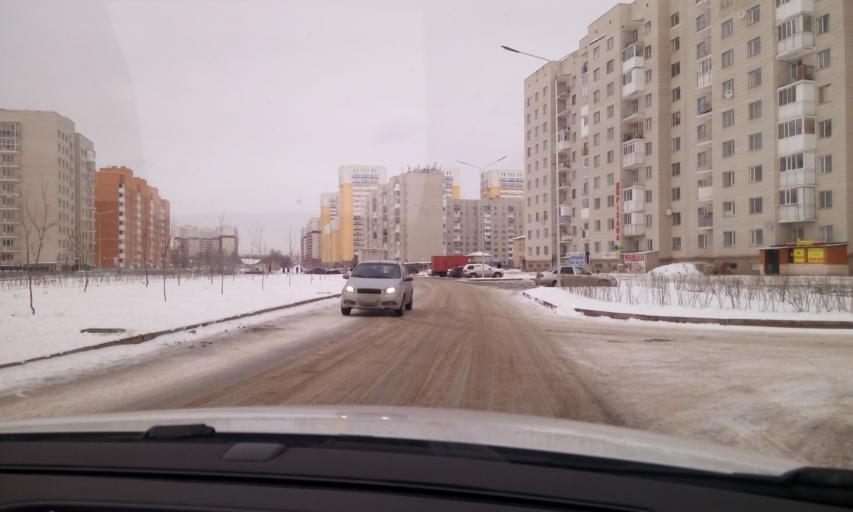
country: KZ
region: Astana Qalasy
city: Astana
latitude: 51.1251
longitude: 71.5052
